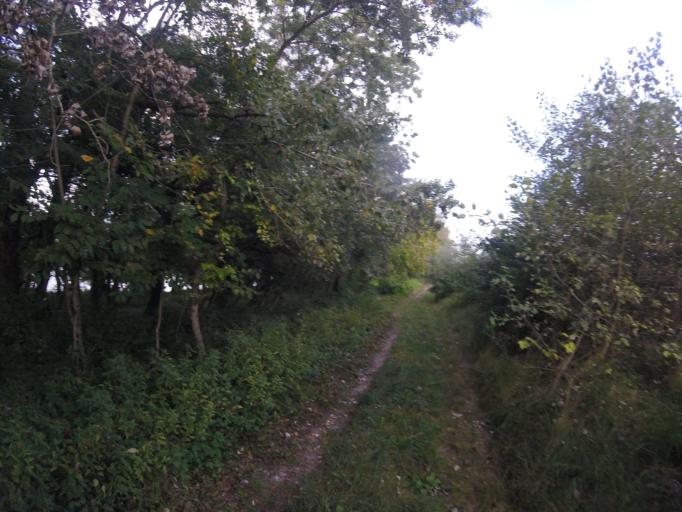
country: HU
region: Pest
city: Szob
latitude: 47.8103
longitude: 18.8523
